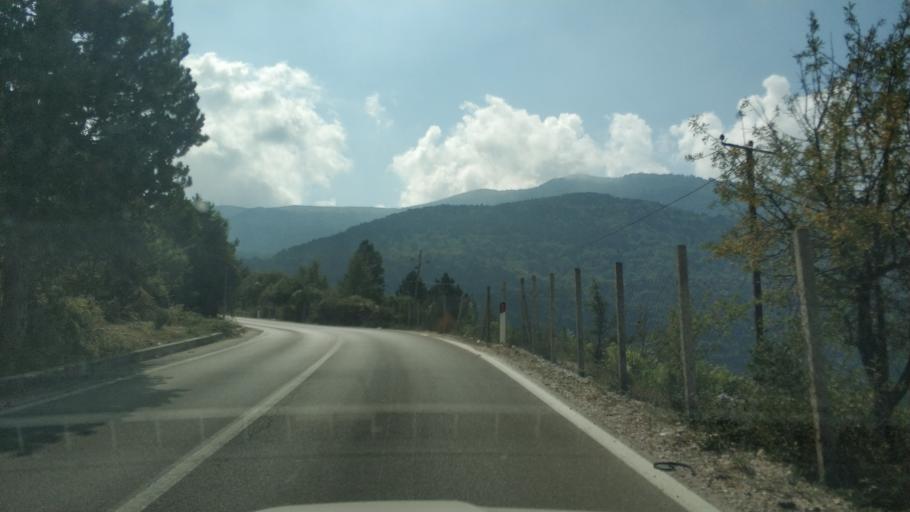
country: AL
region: Vlore
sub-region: Rrethi i Vlores
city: Brataj
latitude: 40.2290
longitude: 19.5779
